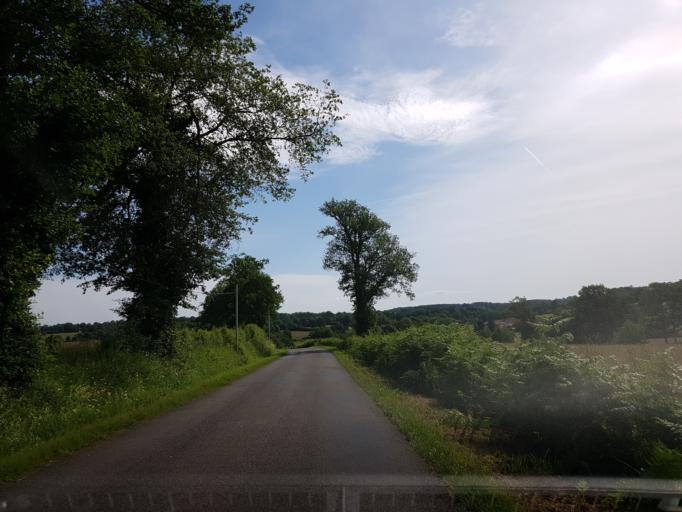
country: FR
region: Poitou-Charentes
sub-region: Departement de la Charente
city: Chabanais
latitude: 45.9271
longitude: 0.7226
